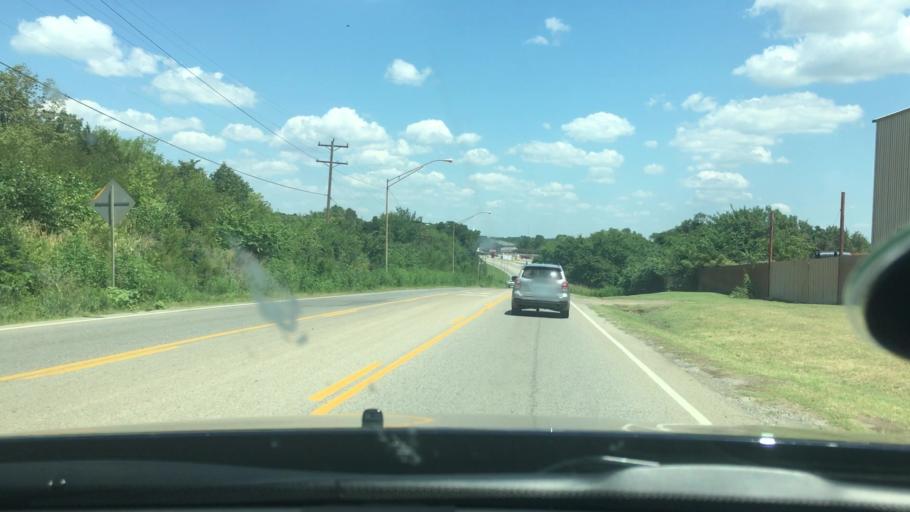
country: US
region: Oklahoma
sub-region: Marshall County
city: Madill
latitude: 34.0725
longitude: -96.7630
